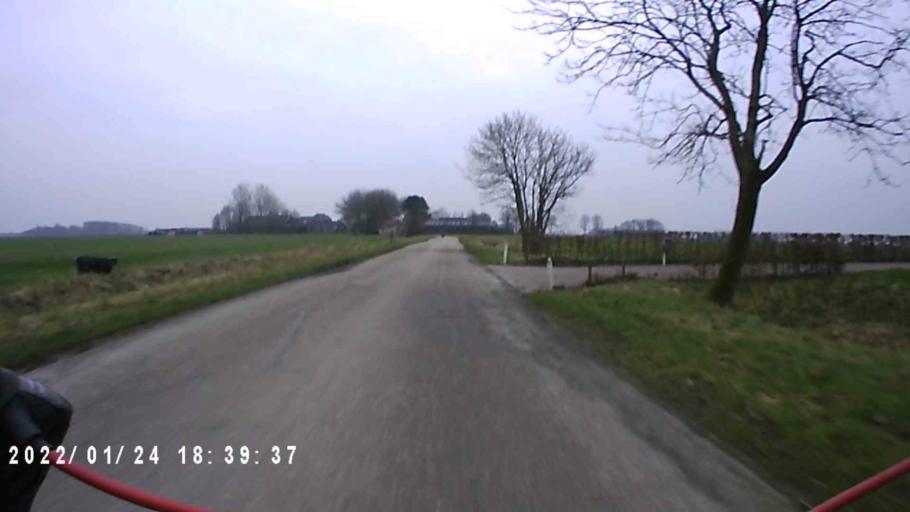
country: NL
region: Groningen
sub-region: Gemeente De Marne
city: Ulrum
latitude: 53.3471
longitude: 6.3411
